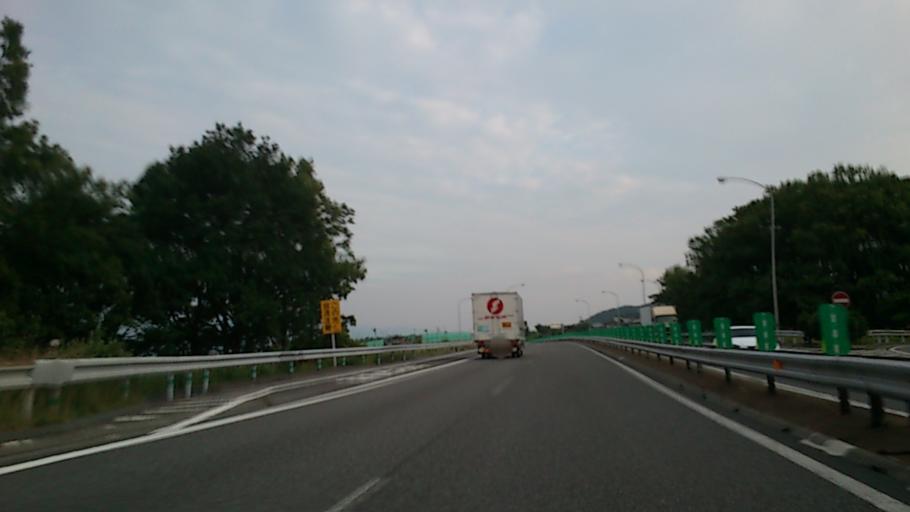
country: JP
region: Nagano
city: Iida
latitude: 35.6153
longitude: 137.8856
